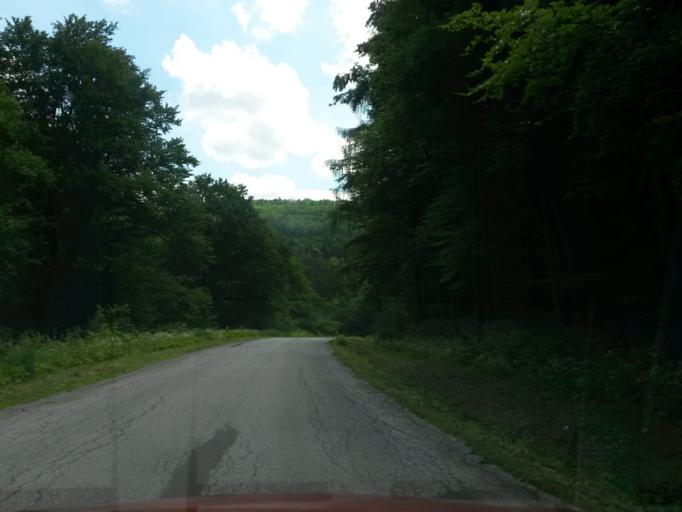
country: SK
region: Kosicky
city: Gelnica
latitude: 48.9236
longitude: 21.0394
